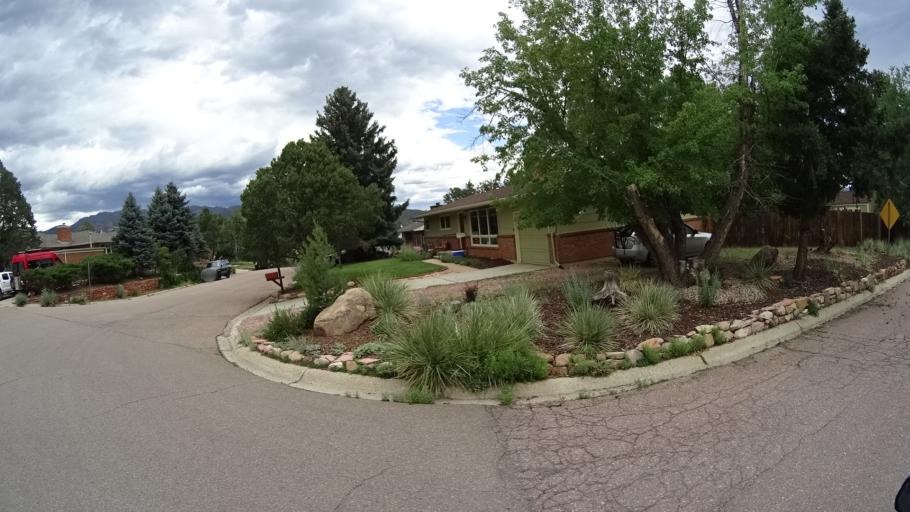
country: US
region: Colorado
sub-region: El Paso County
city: Manitou Springs
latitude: 38.8500
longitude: -104.8934
